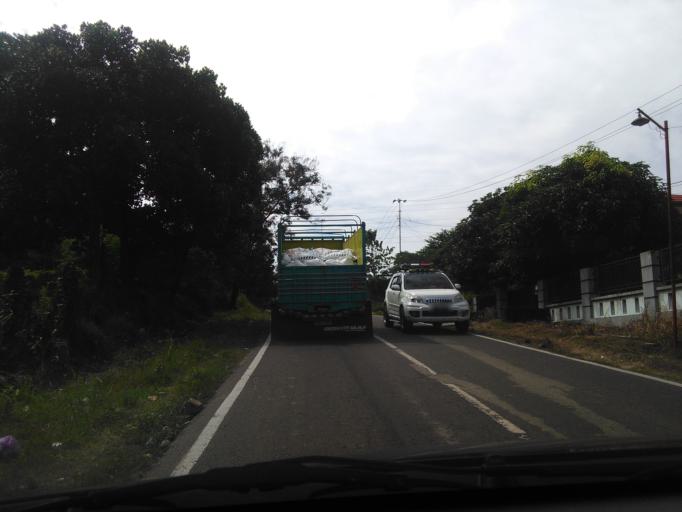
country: ID
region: South Sulawesi
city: Harapankarya
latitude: -3.9743
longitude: 119.6382
